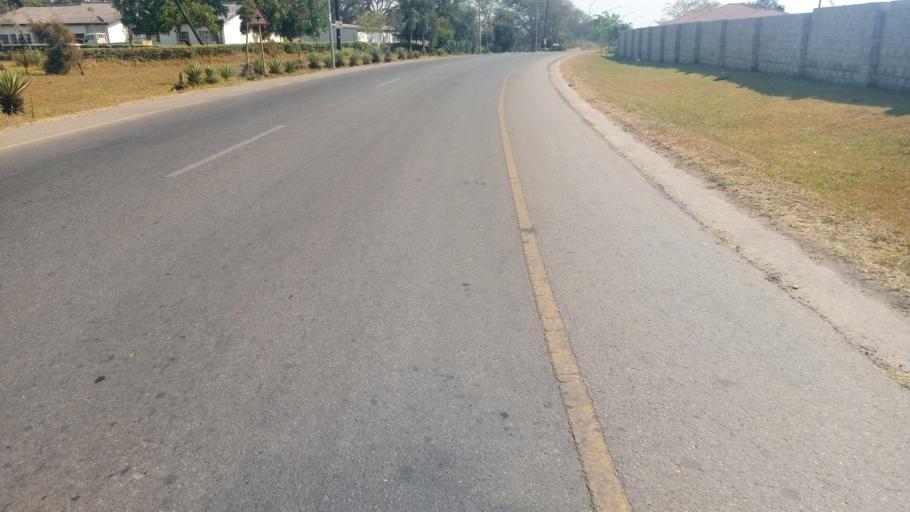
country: ZM
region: Lusaka
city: Lusaka
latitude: -15.4560
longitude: 28.4341
